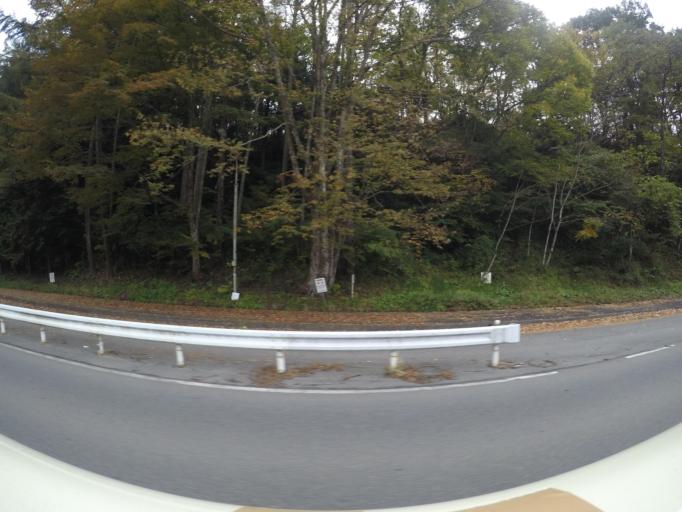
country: JP
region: Nagano
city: Chino
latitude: 35.8788
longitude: 138.0950
